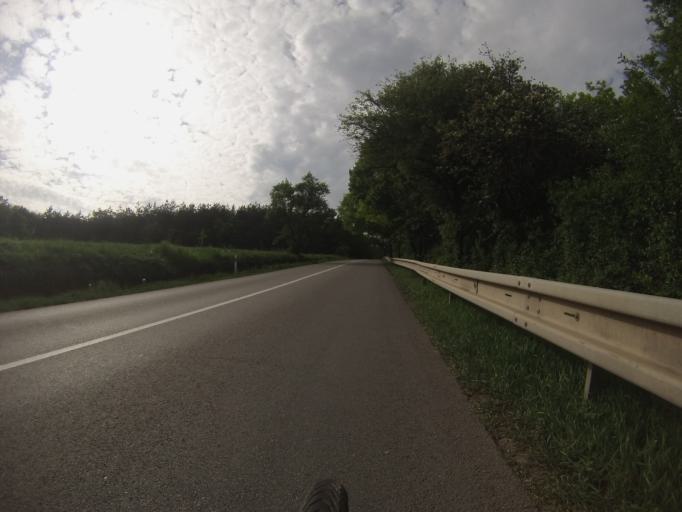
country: CZ
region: South Moravian
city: Veverska Bityska
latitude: 49.2558
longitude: 16.4502
